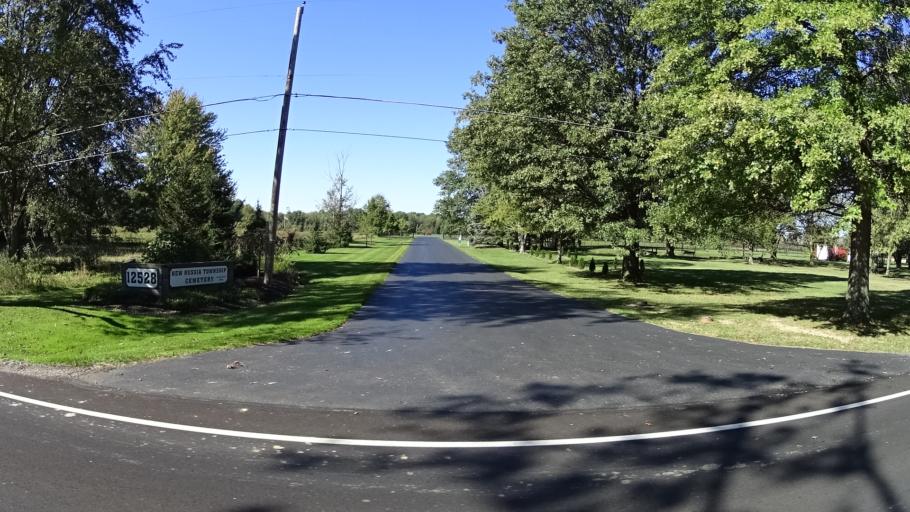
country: US
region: Ohio
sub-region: Lorain County
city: Oberlin
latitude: 41.3025
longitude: -82.1969
